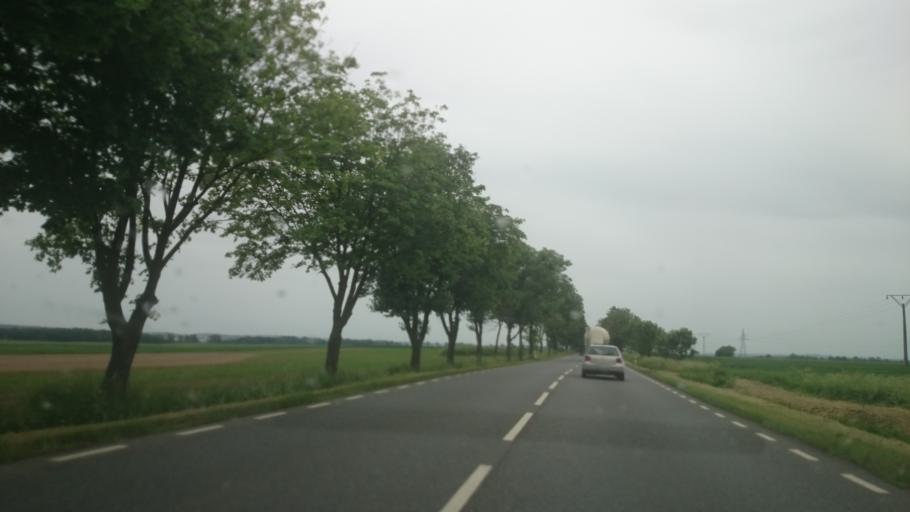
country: PL
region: Opole Voivodeship
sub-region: Powiat nyski
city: Paczkow
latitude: 50.4532
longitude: 17.0491
